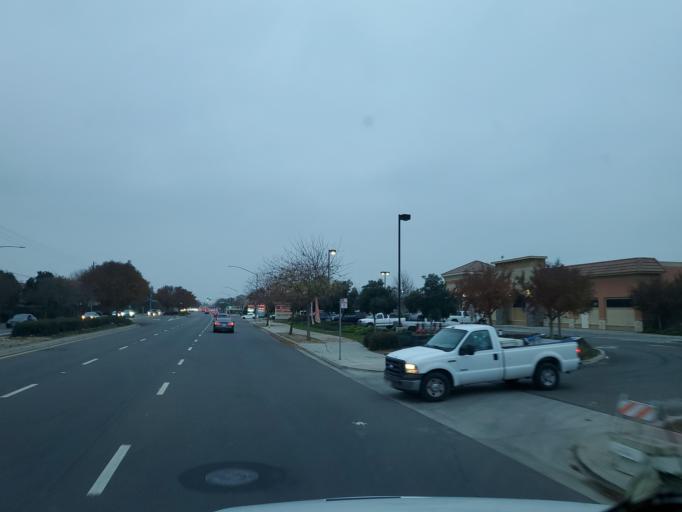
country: US
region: California
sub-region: Stanislaus County
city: Salida
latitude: 37.7003
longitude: -121.0609
